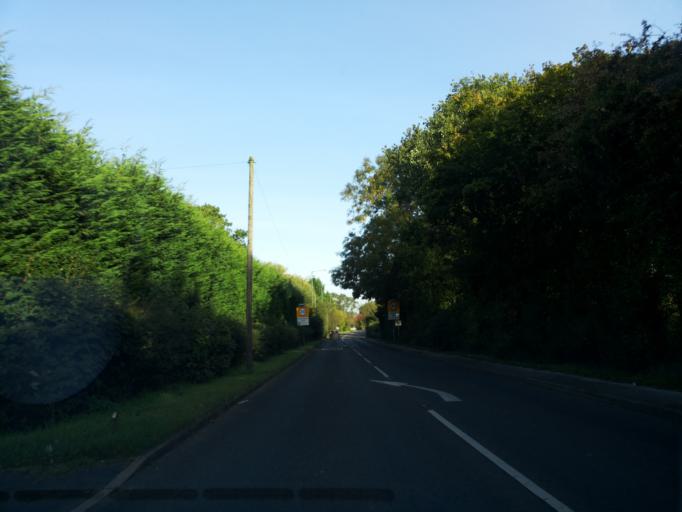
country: GB
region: England
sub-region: Warwickshire
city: Wroxall
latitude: 52.3497
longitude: -1.6931
